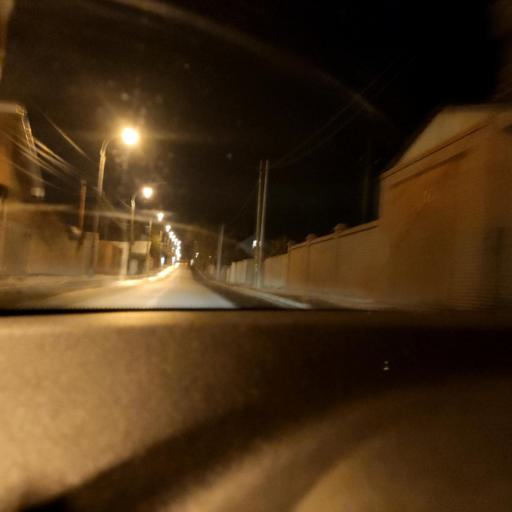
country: RU
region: Samara
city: Samara
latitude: 53.2665
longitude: 50.2043
